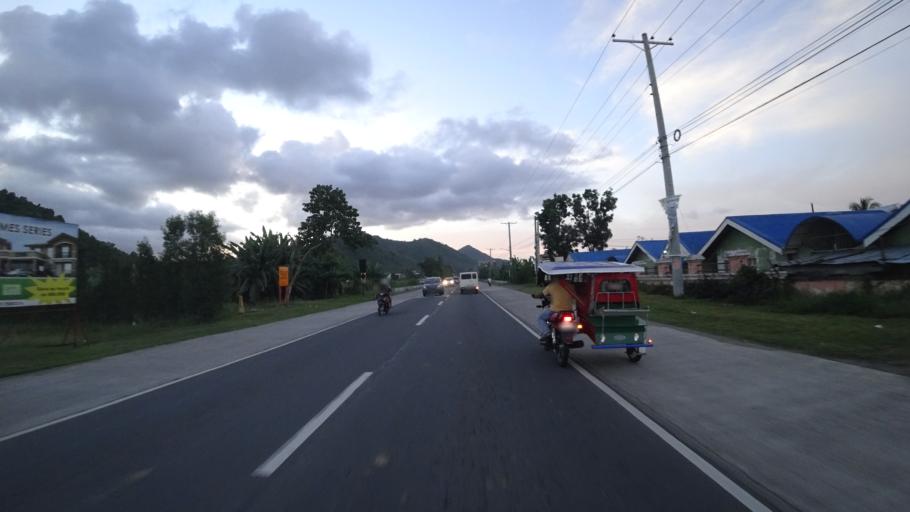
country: PH
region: Eastern Visayas
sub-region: Province of Leyte
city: Pawing
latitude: 11.1882
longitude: 124.9950
